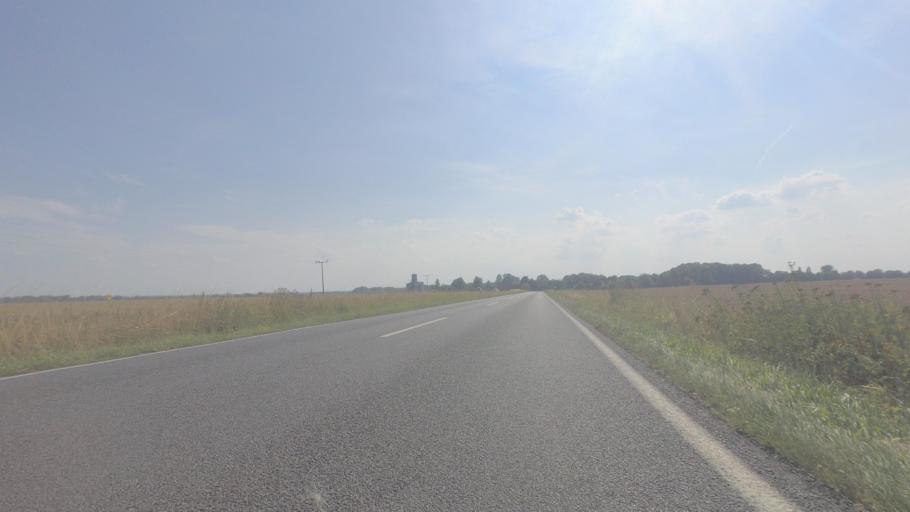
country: DE
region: Mecklenburg-Vorpommern
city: Wittenhagen
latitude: 54.1347
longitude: 13.1441
